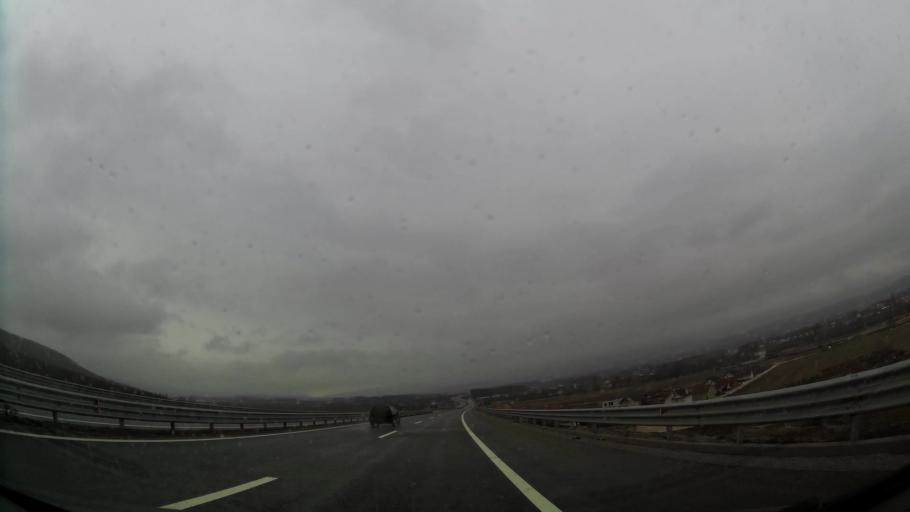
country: XK
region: Ferizaj
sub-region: Komuna e Ferizajt
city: Ferizaj
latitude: 42.3159
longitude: 21.2081
